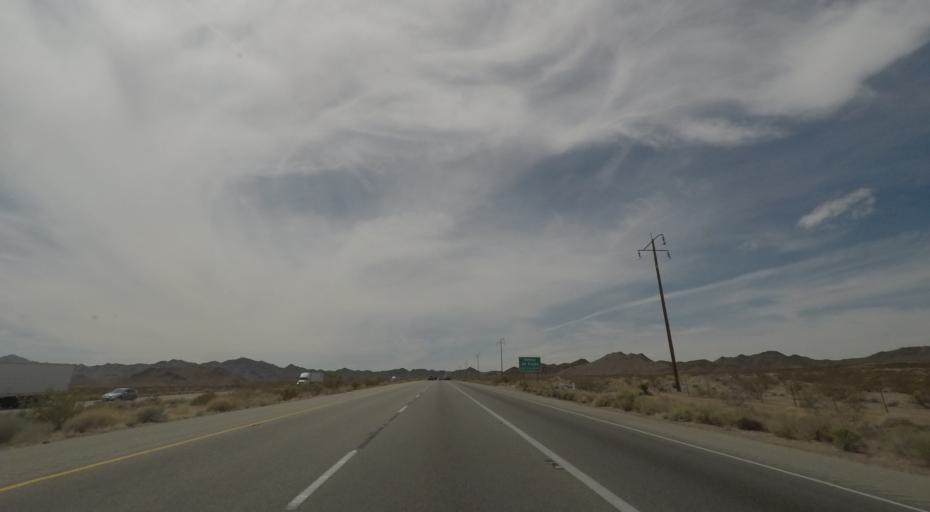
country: US
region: California
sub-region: San Bernardino County
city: Needles
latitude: 34.8333
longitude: -115.0136
